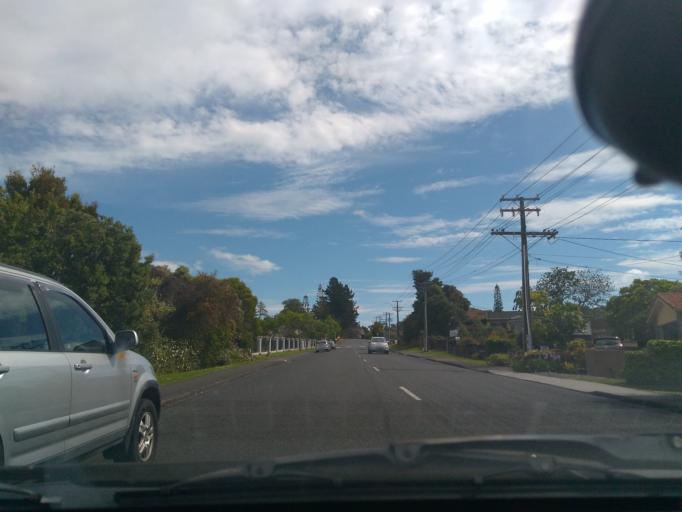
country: NZ
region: Auckland
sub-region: Auckland
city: Titirangi
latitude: -36.9345
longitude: 174.6724
